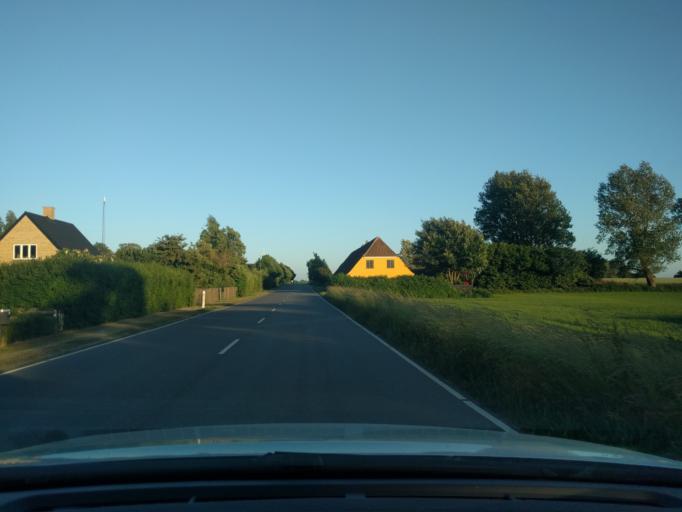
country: DK
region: South Denmark
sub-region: Kerteminde Kommune
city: Kerteminde
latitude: 55.5433
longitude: 10.6592
